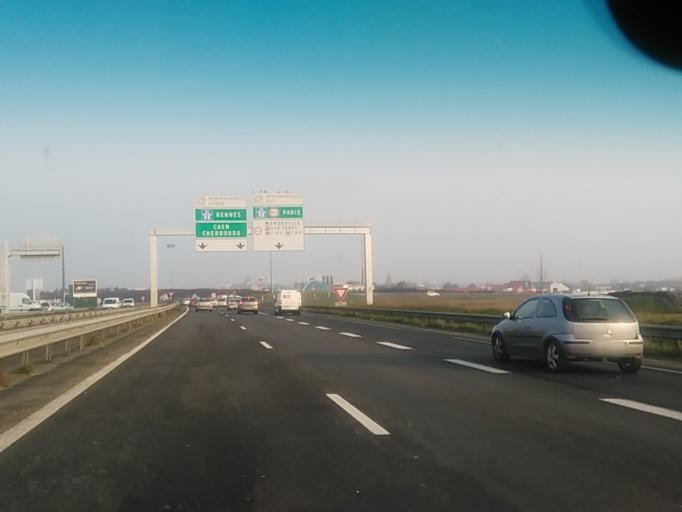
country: FR
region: Lower Normandy
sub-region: Departement du Calvados
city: Ifs
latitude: 49.1434
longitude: -0.3375
